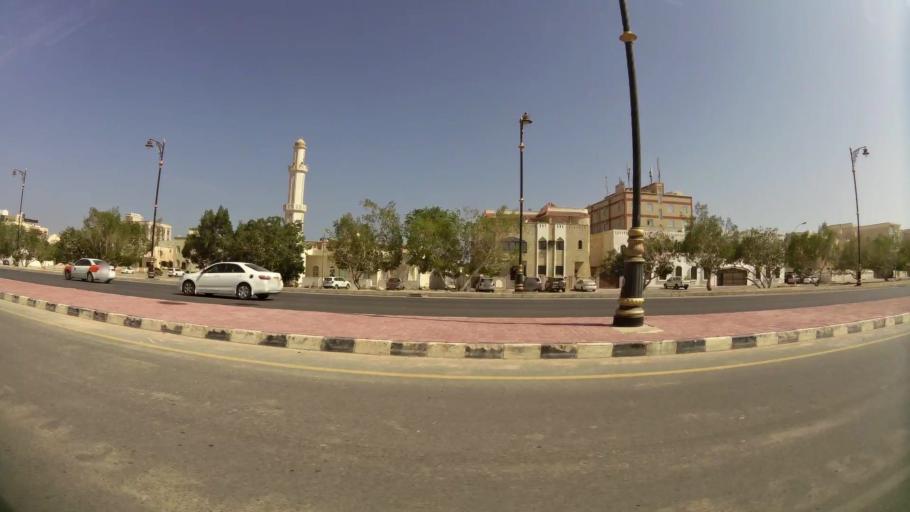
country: OM
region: Zufar
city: Salalah
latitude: 17.0233
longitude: 54.0809
